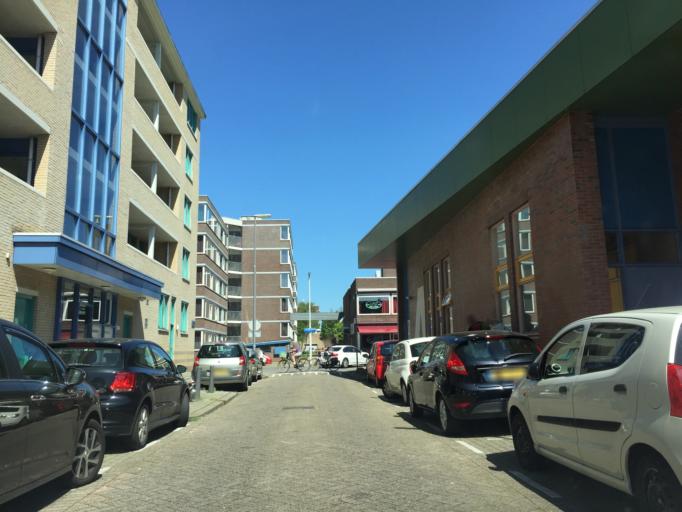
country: NL
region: South Holland
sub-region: Gemeente Rotterdam
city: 's-Gravenland
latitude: 51.9415
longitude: 4.5469
